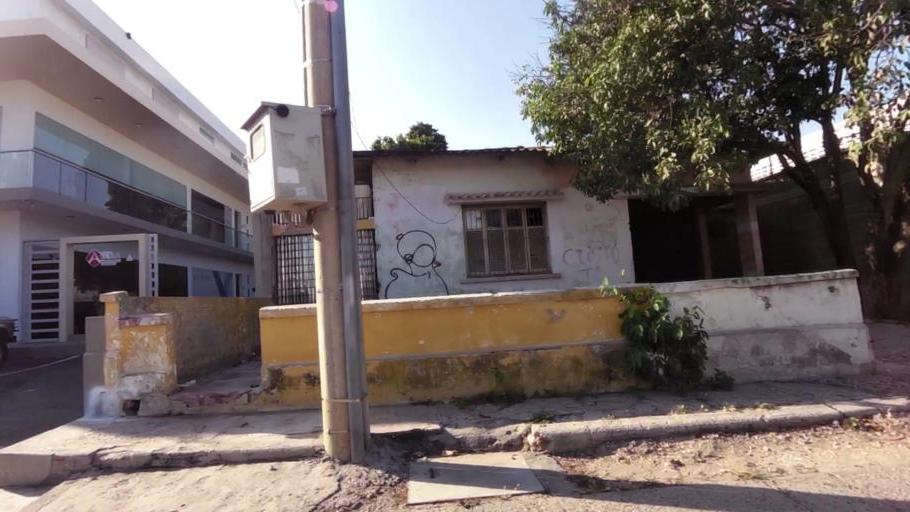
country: CO
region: Bolivar
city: Cartagena
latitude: 10.3964
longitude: -75.5211
